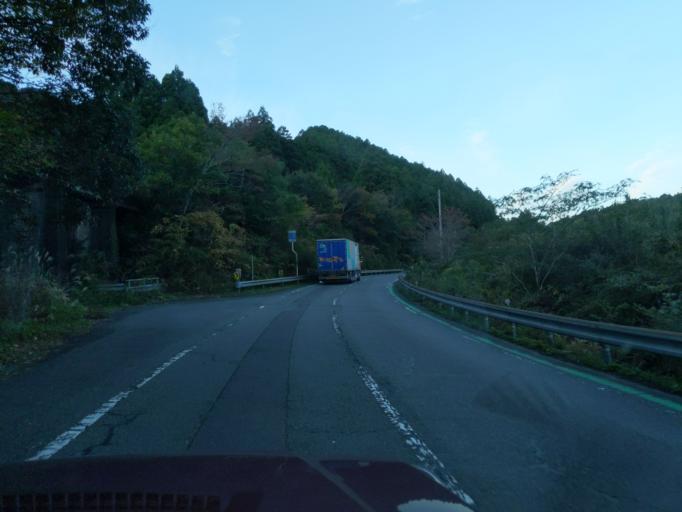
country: JP
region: Tokushima
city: Anan
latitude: 33.7090
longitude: 134.4693
